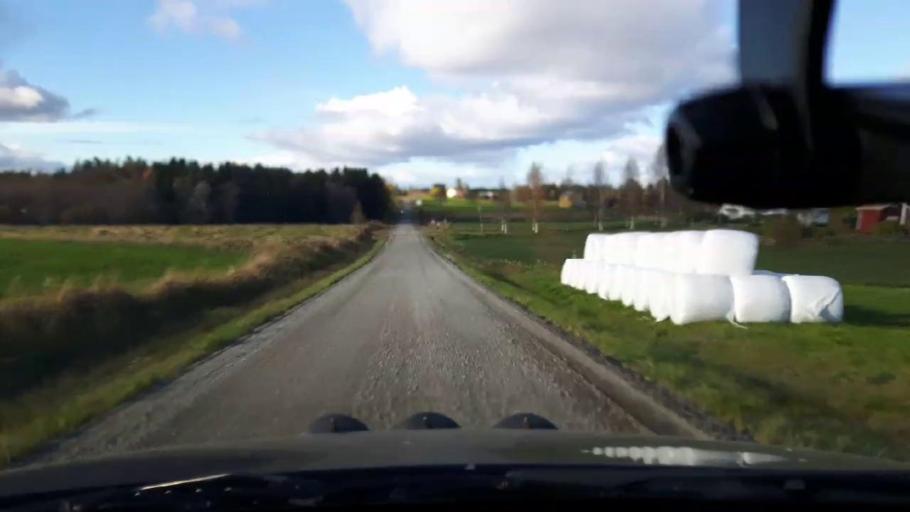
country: SE
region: Jaemtland
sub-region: Bergs Kommun
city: Hoverberg
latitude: 63.0212
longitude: 14.3021
